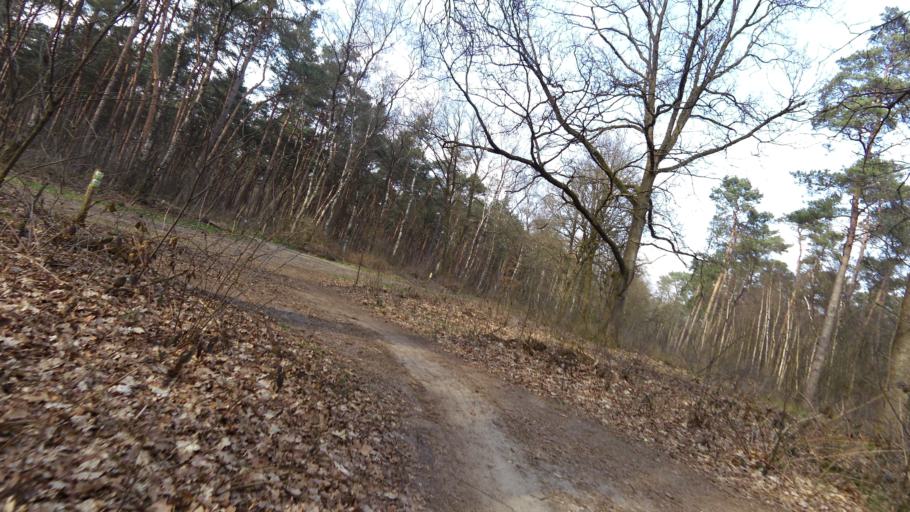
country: NL
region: Gelderland
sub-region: Gemeente Ede
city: Otterlo
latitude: 52.0895
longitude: 5.7602
